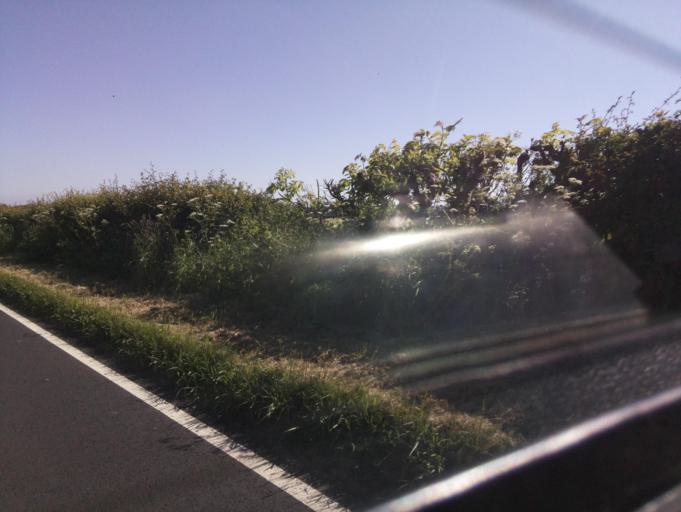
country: GB
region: Scotland
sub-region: Fife
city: Balmullo
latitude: 56.3624
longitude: -2.9393
